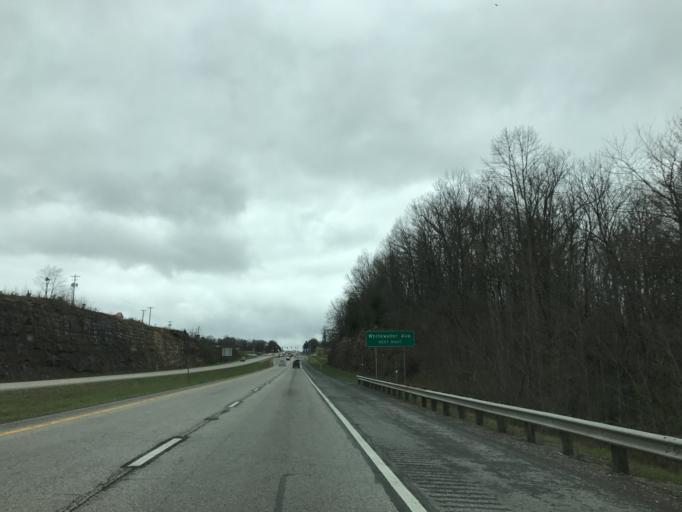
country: US
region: West Virginia
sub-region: Fayette County
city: Fayetteville
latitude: 38.0361
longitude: -81.1229
